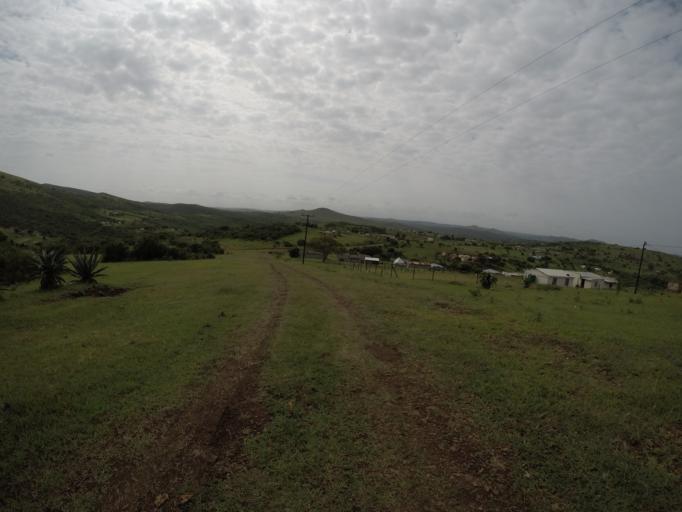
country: ZA
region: KwaZulu-Natal
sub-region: uThungulu District Municipality
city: Empangeni
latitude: -28.6160
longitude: 31.8991
